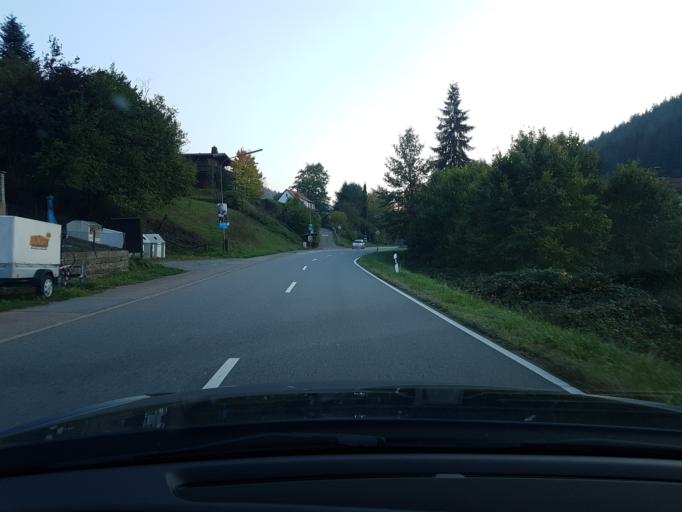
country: DE
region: Hesse
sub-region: Regierungsbezirk Darmstadt
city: Rothenberg
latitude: 49.5166
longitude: 8.9659
